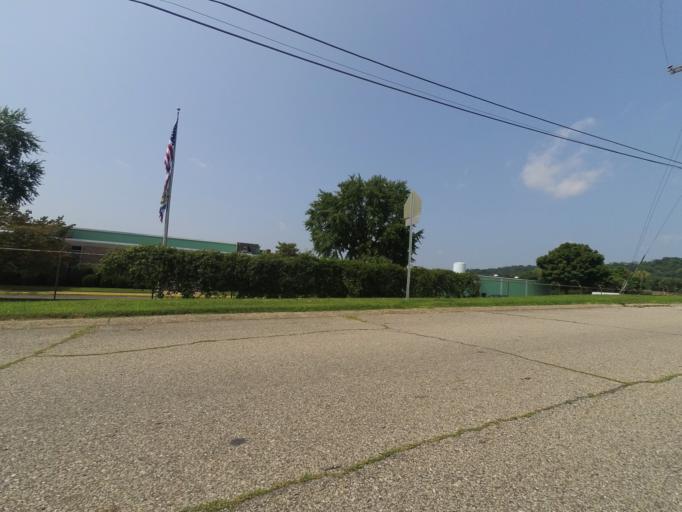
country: US
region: West Virginia
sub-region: Cabell County
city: Huntington
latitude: 38.4302
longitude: -82.4137
